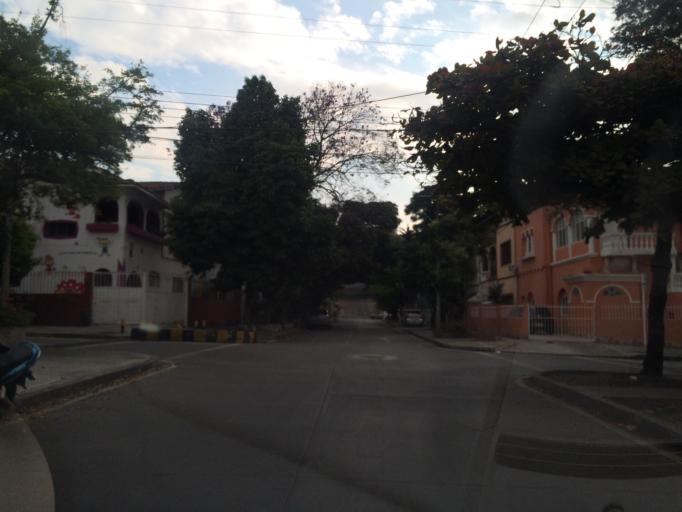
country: CO
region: Valle del Cauca
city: Cali
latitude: 3.4375
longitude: -76.5449
